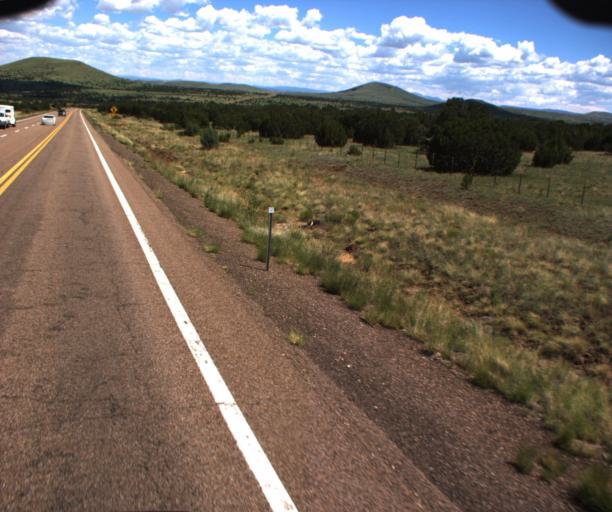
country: US
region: Arizona
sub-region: Apache County
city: Springerville
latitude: 34.2647
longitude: -109.5691
